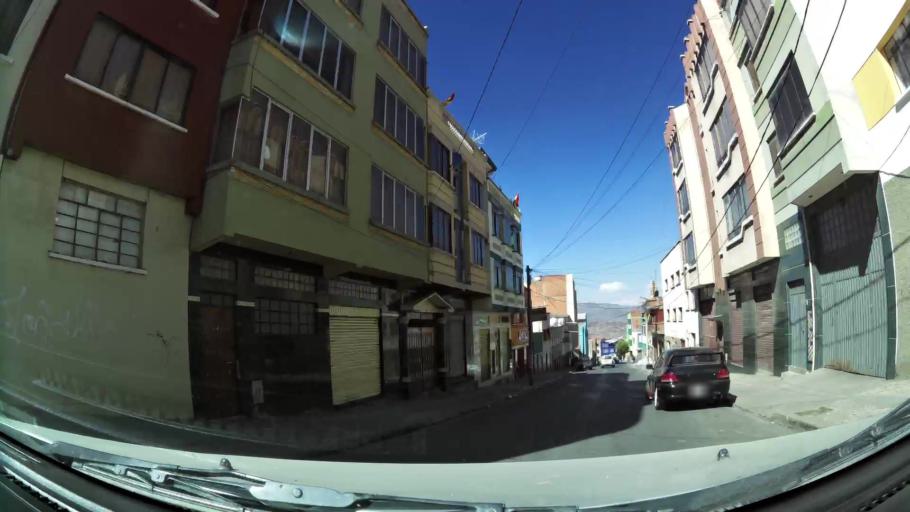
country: BO
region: La Paz
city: La Paz
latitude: -16.4925
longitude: -68.1564
